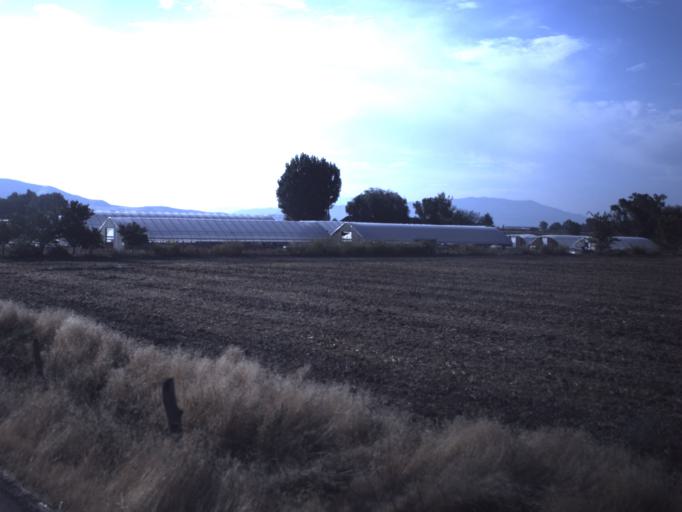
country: US
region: Utah
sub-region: Utah County
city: Benjamin
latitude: 40.0854
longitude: -111.7059
